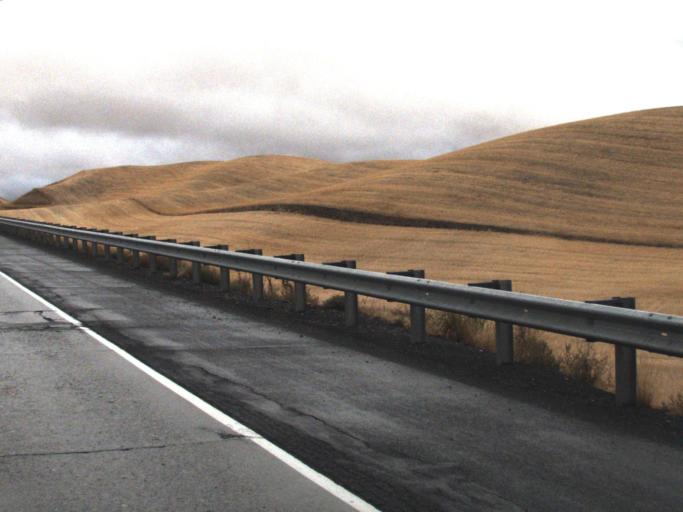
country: US
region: Washington
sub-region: Whitman County
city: Colfax
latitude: 47.0973
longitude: -117.3789
